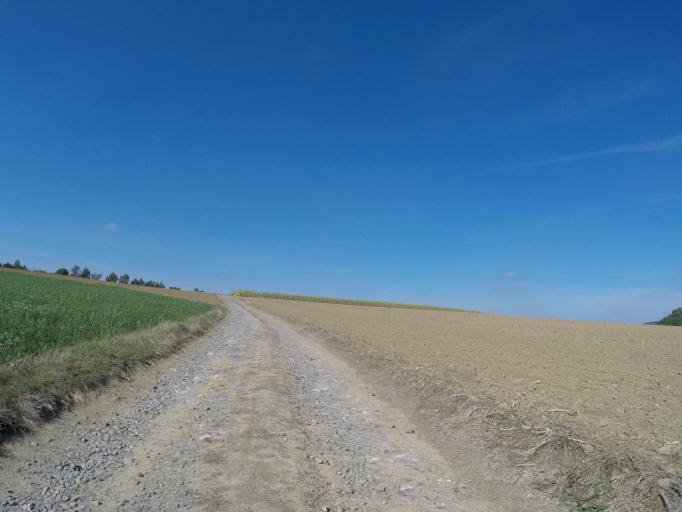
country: BE
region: Wallonia
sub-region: Province de Namur
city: Assesse
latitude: 50.3060
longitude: 5.0231
